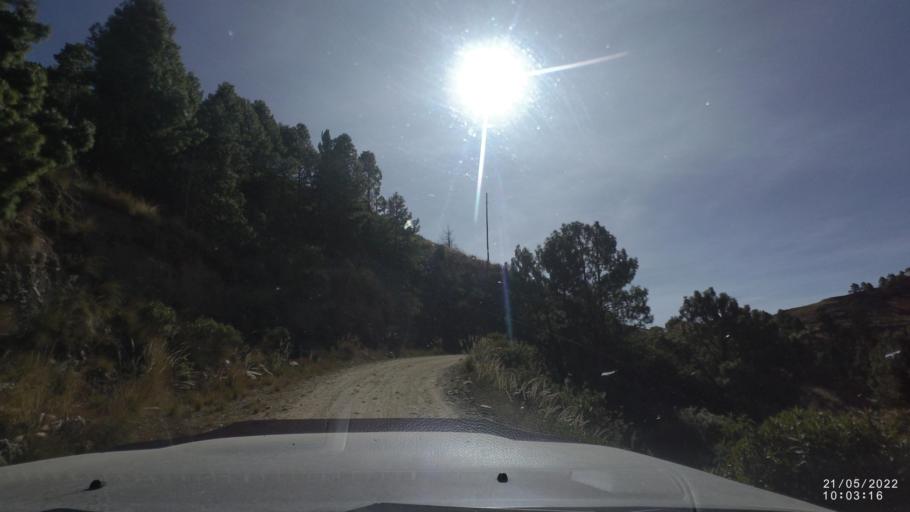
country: BO
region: Cochabamba
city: Colomi
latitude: -17.3405
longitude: -65.9901
